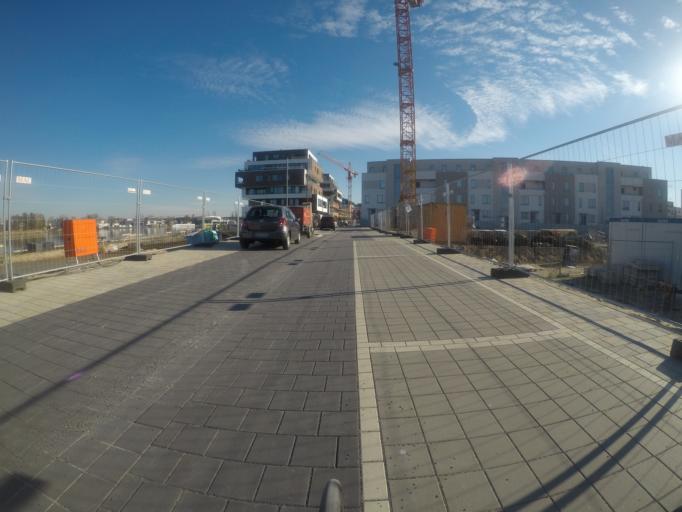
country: DE
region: Berlin
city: Grunau
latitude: 52.4264
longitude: 13.5765
